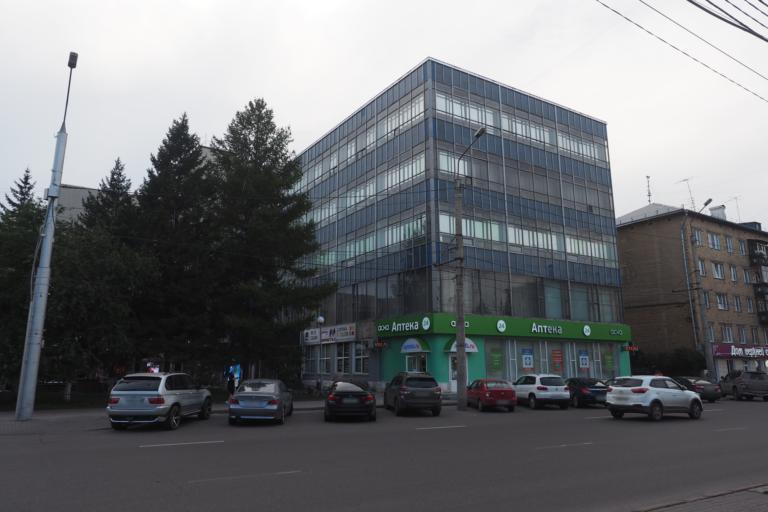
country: RU
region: Krasnoyarskiy
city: Krasnoyarsk
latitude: 56.0125
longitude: 92.8761
